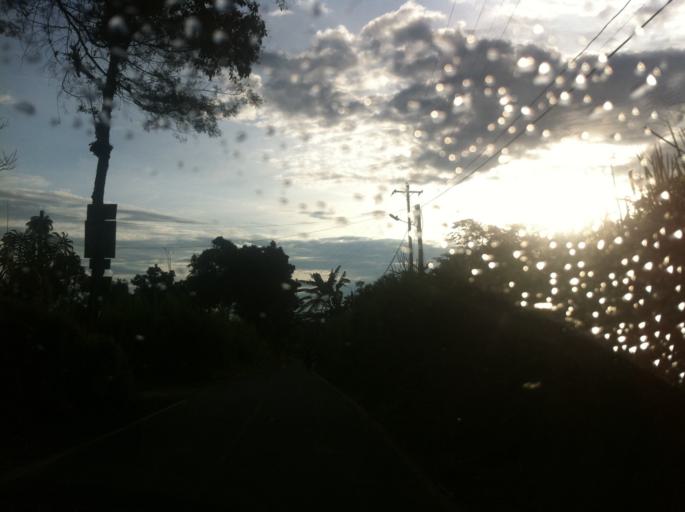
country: CO
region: Quindio
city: Circasia
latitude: 4.5838
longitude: -75.6346
